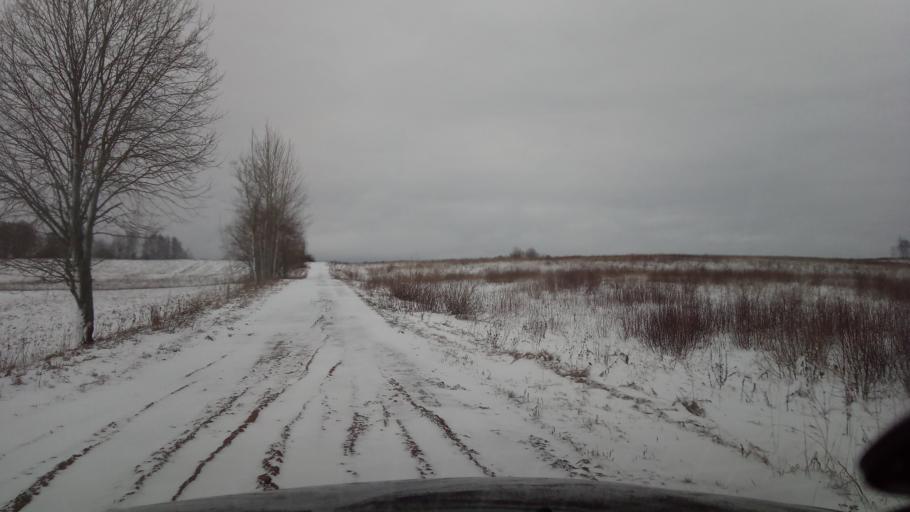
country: LT
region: Utenos apskritis
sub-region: Utena
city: Utena
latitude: 55.6107
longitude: 25.8665
